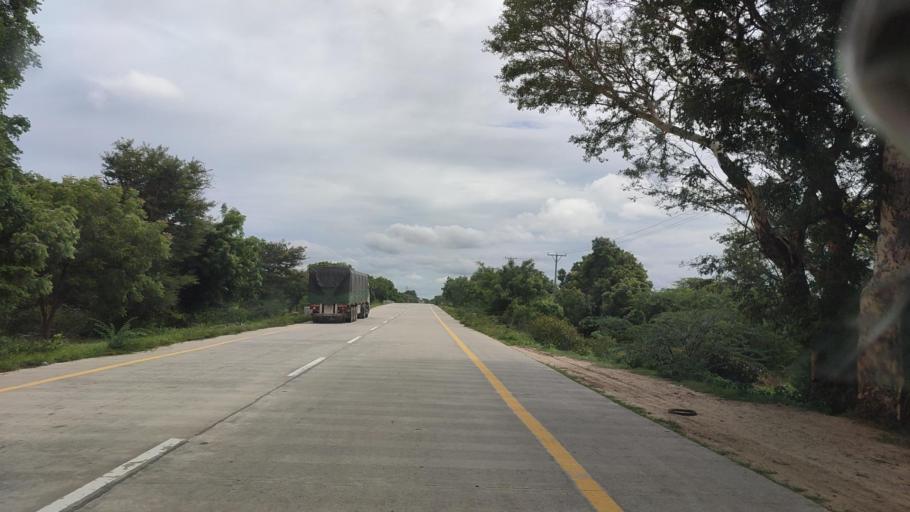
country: MM
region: Mandalay
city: Meiktila
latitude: 21.0631
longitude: 96.0047
